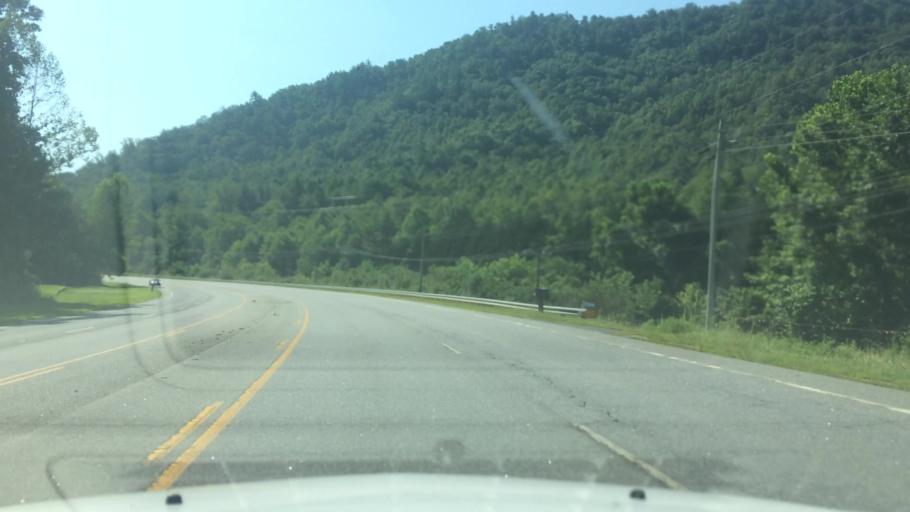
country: US
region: North Carolina
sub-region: Caldwell County
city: Lenoir
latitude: 36.0281
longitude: -81.5877
